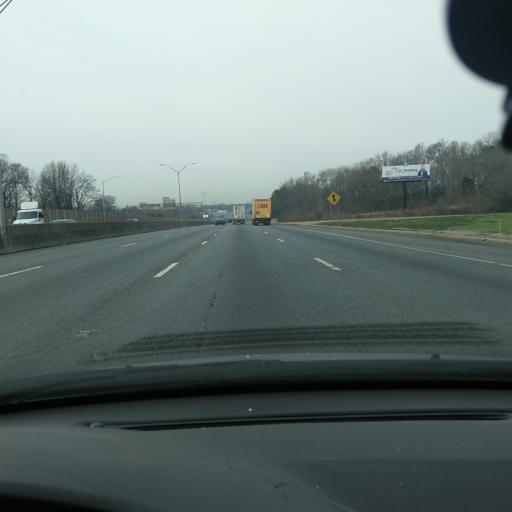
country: US
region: North Carolina
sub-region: Mecklenburg County
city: Charlotte
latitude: 35.2711
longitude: -80.8559
